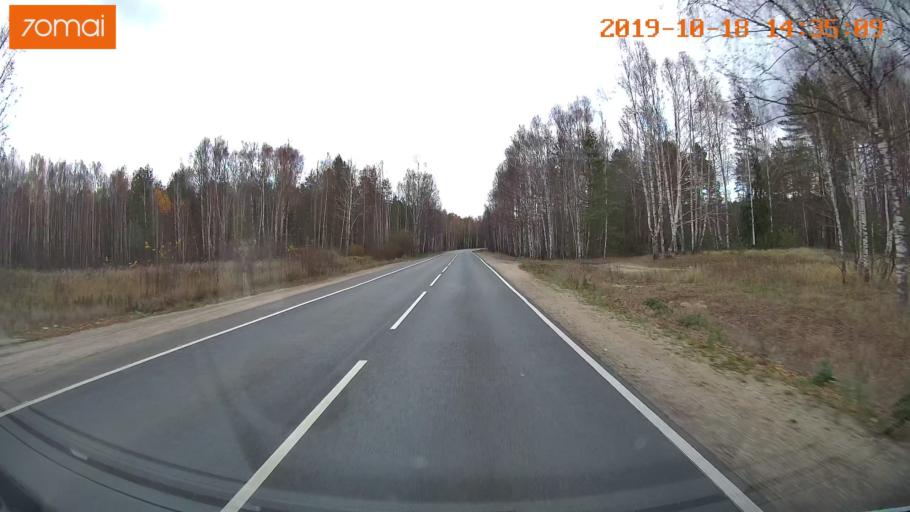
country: RU
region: Vladimir
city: Velikodvorskiy
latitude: 55.2202
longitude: 40.6308
